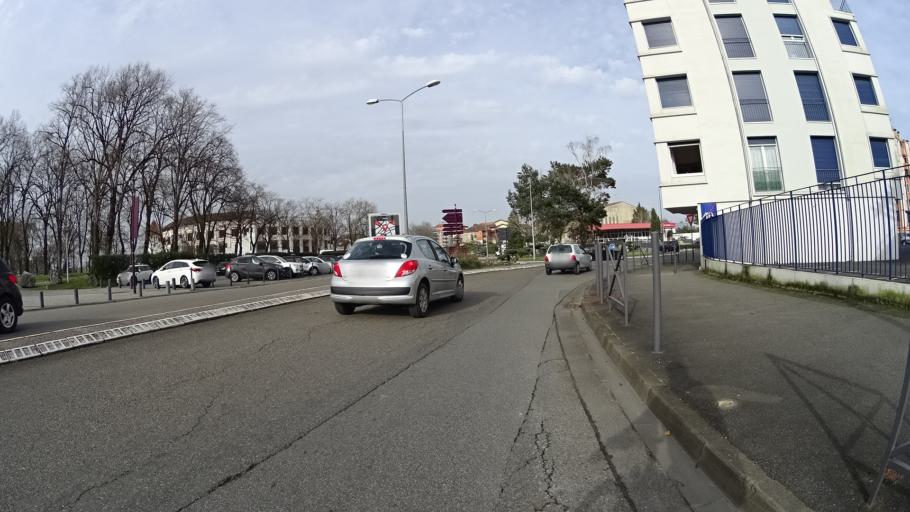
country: FR
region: Aquitaine
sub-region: Departement des Landes
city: Dax
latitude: 43.7115
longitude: -1.0499
